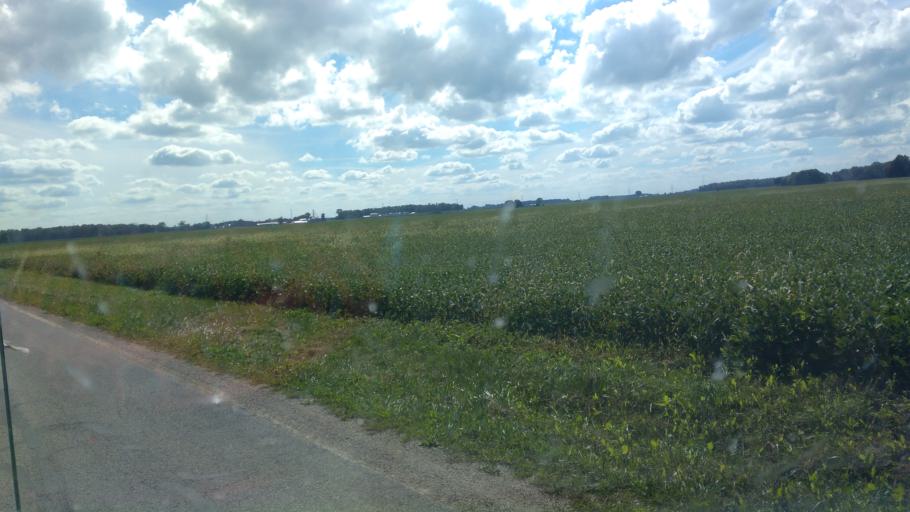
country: US
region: Ohio
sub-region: Ottawa County
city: Port Clinton
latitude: 41.4083
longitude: -82.8826
